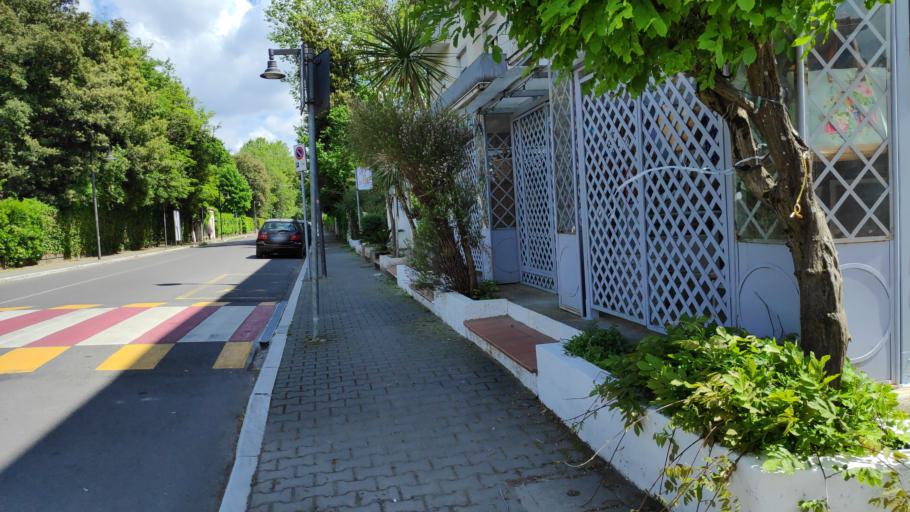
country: IT
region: Tuscany
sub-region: Provincia di Massa-Carrara
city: Massa
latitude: 43.9965
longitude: 10.1193
